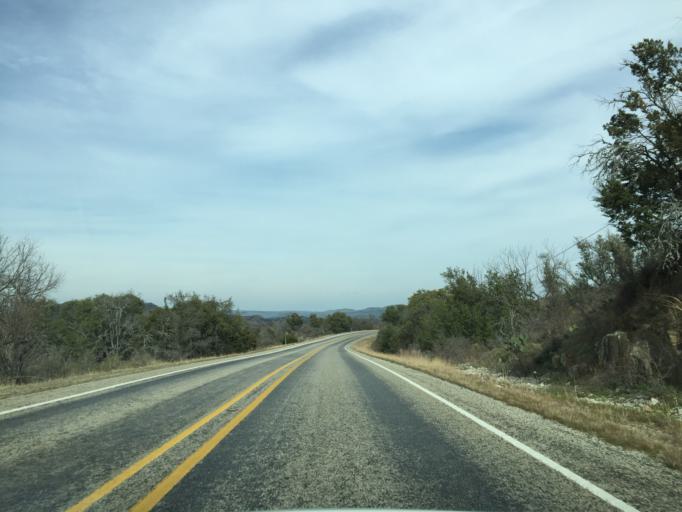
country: US
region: Texas
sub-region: Gillespie County
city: Fredericksburg
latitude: 30.4625
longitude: -98.7262
